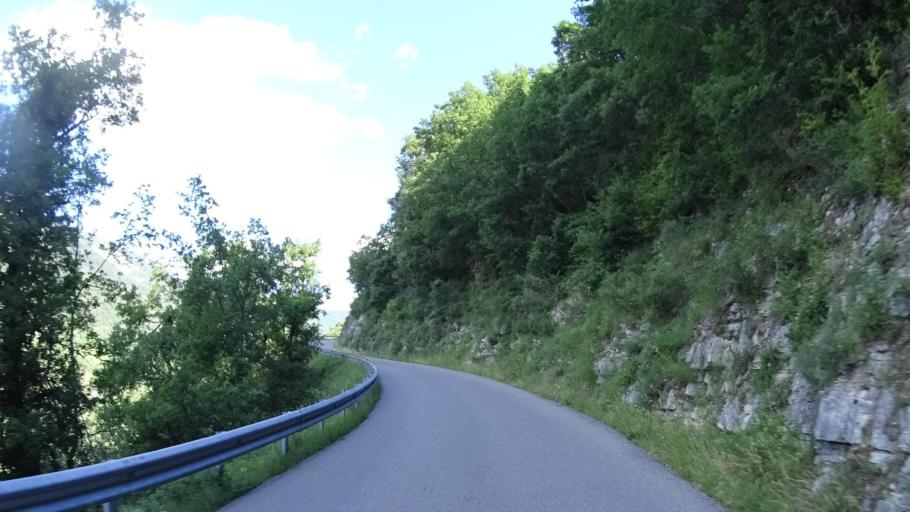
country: FR
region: Provence-Alpes-Cote d'Azur
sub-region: Departement des Alpes-de-Haute-Provence
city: Annot
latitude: 44.0163
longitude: 6.6343
